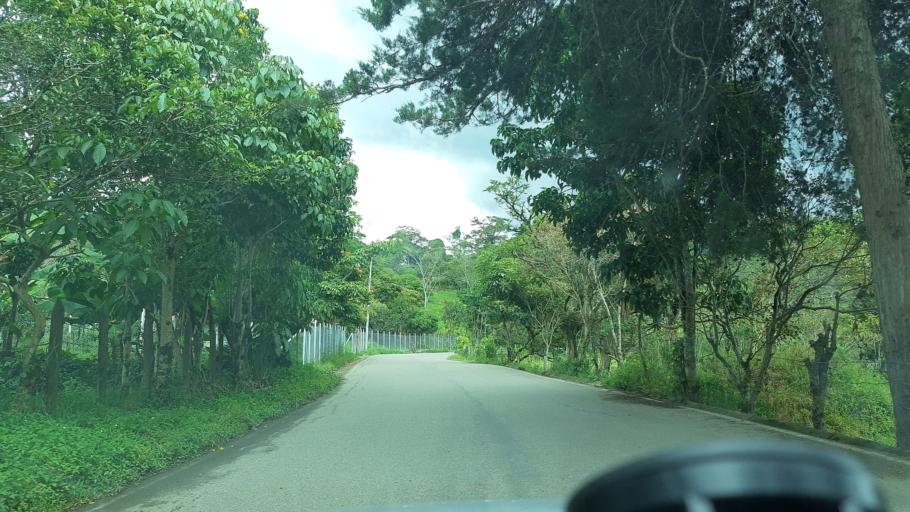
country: CO
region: Boyaca
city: Garagoa
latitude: 5.0963
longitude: -73.3676
